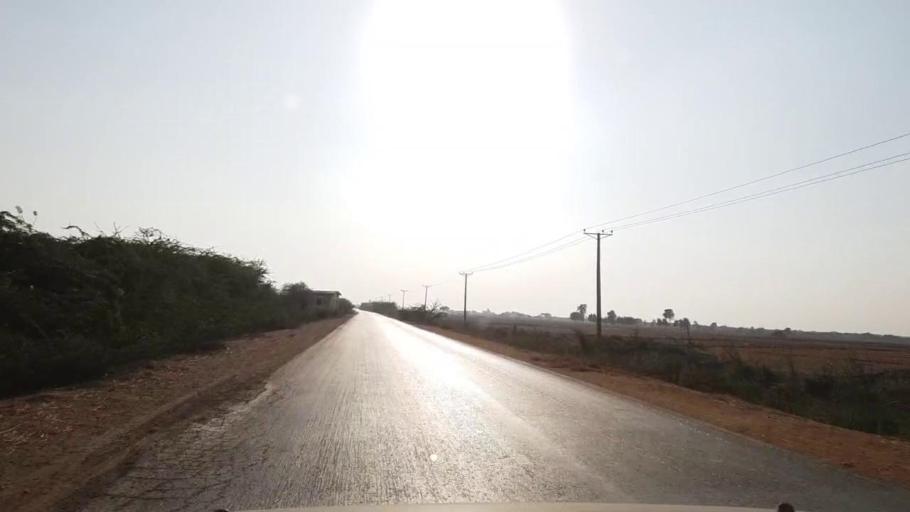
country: PK
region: Sindh
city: Bulri
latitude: 24.8015
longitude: 68.3082
